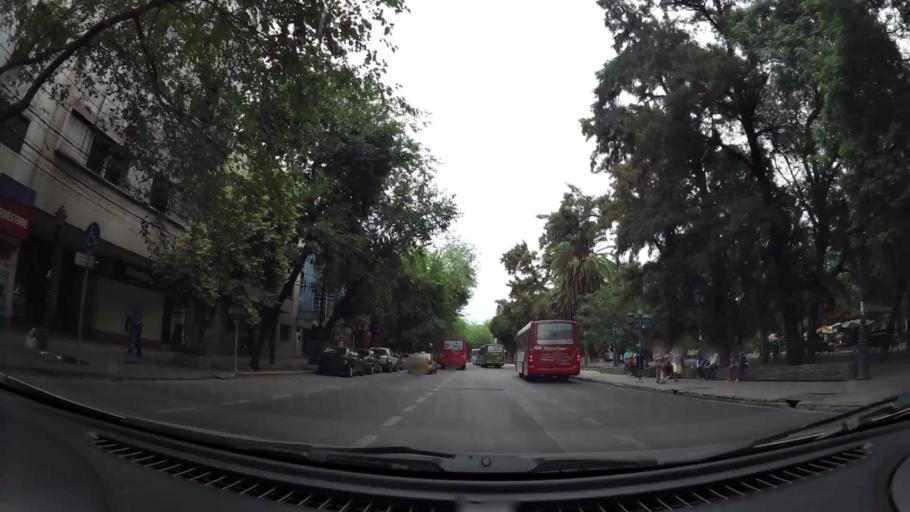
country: AR
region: Mendoza
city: Mendoza
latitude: -32.8903
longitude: -68.8434
